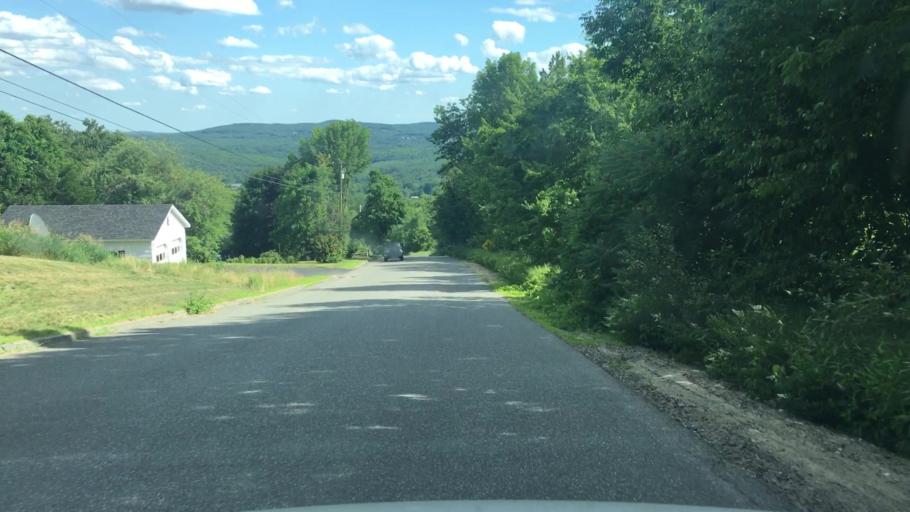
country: US
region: Maine
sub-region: Franklin County
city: Wilton
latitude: 44.6321
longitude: -70.1975
